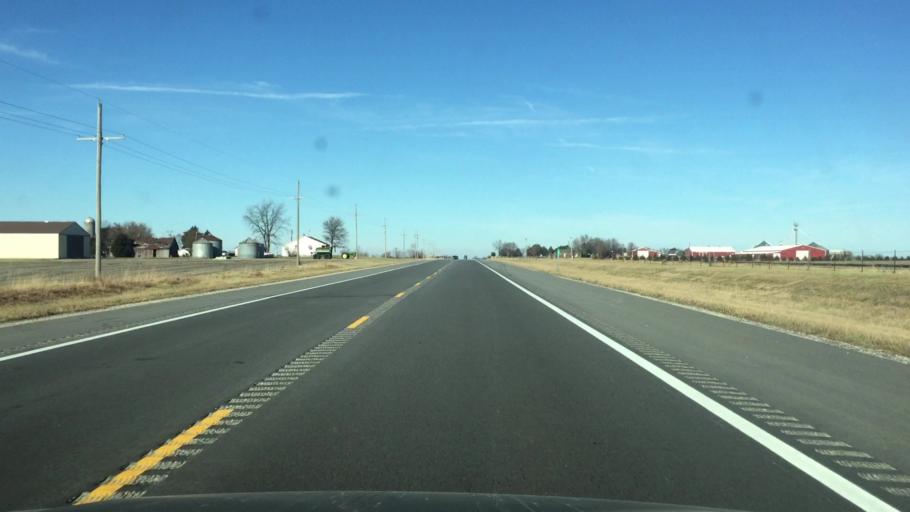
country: US
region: Kansas
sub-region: Franklin County
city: Ottawa
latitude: 38.5028
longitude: -95.2675
